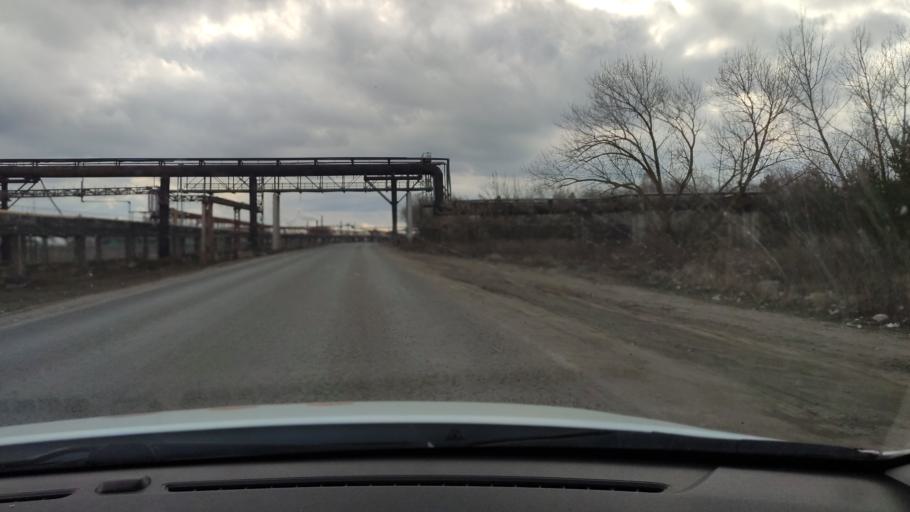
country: RU
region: Tatarstan
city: Staroye Arakchino
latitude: 55.8801
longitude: 48.9761
